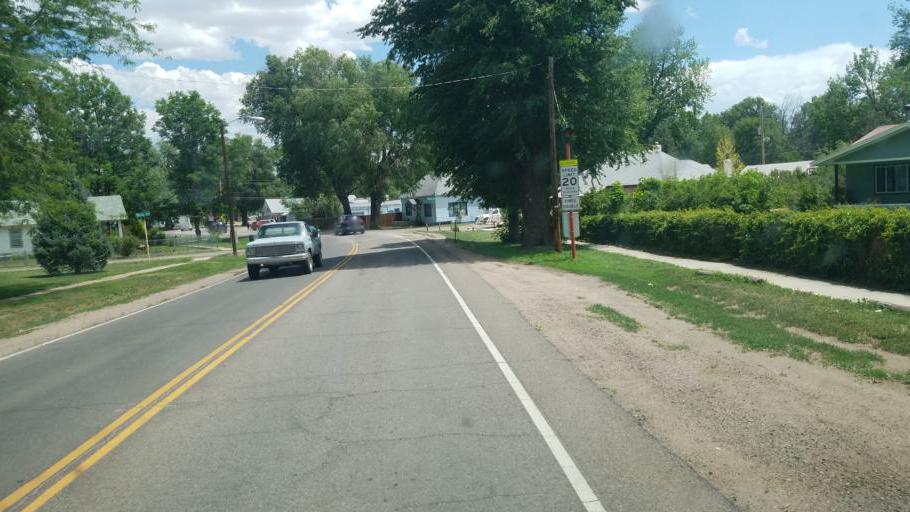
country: US
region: Colorado
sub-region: Fremont County
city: Florence
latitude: 38.3957
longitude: -105.1272
